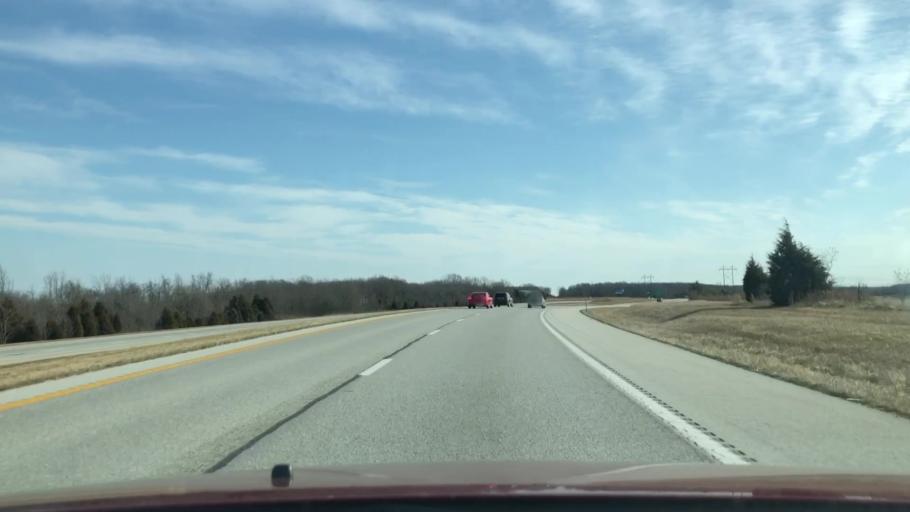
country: US
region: Missouri
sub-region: Webster County
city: Seymour
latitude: 37.1183
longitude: -92.6860
